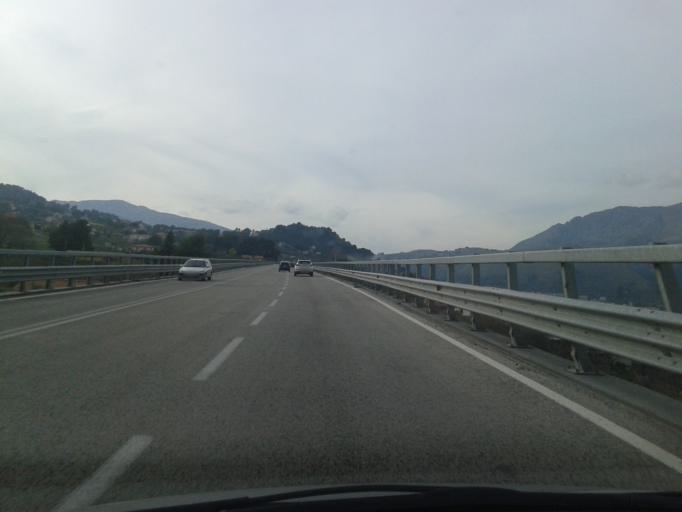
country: IT
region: Sicily
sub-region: Palermo
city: Giacalone
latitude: 38.0342
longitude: 13.2504
